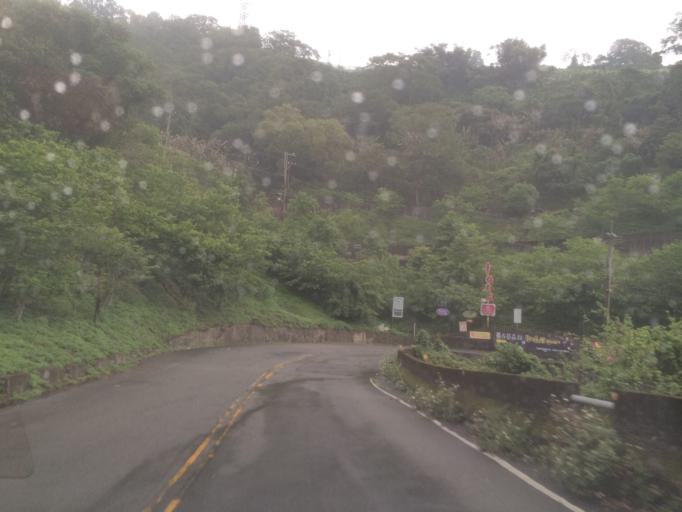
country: TW
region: Taiwan
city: Fengyuan
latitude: 24.1702
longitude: 120.8226
